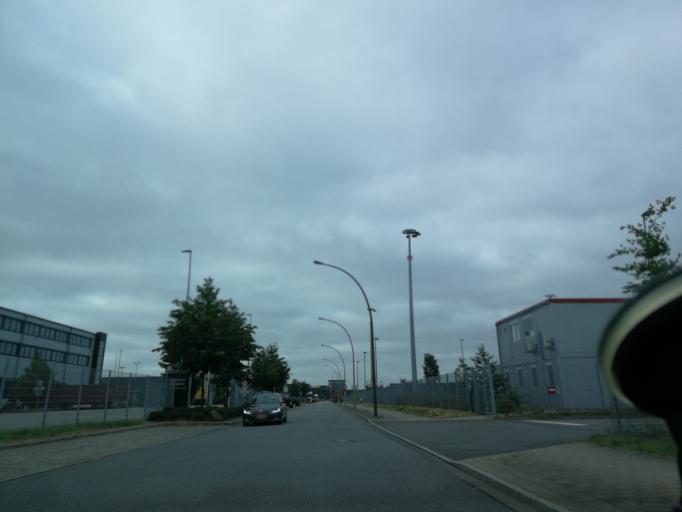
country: DE
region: Hamburg
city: Altona
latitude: 53.5048
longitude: 9.9217
